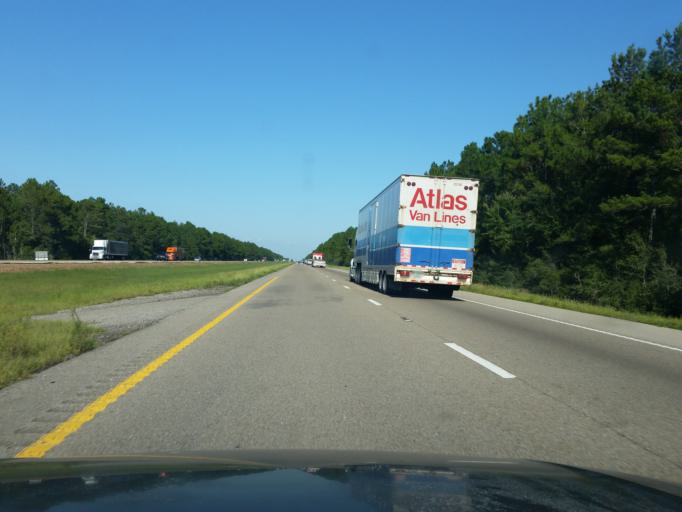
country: US
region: Mississippi
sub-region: Hancock County
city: Kiln
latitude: 30.3488
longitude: -89.4535
